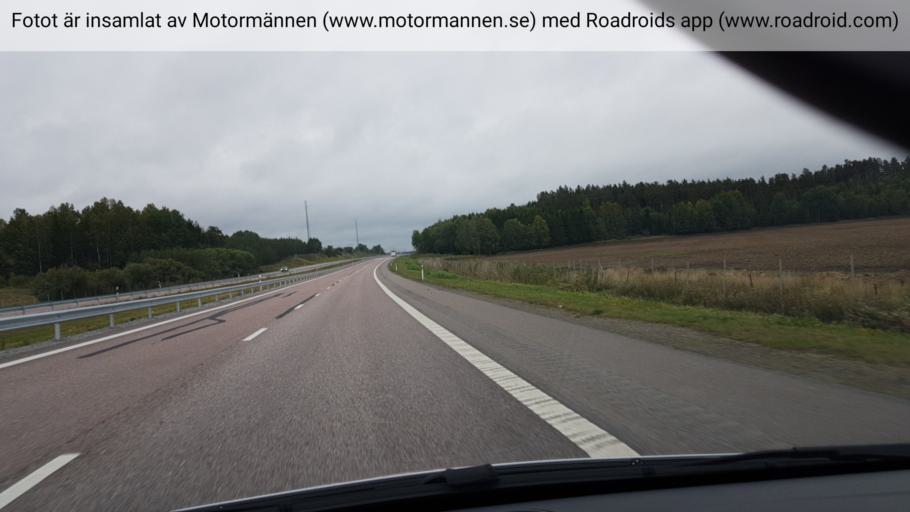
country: SE
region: Soedermanland
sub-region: Strangnas Kommun
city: Akers Styckebruk
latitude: 59.2979
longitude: 17.0914
